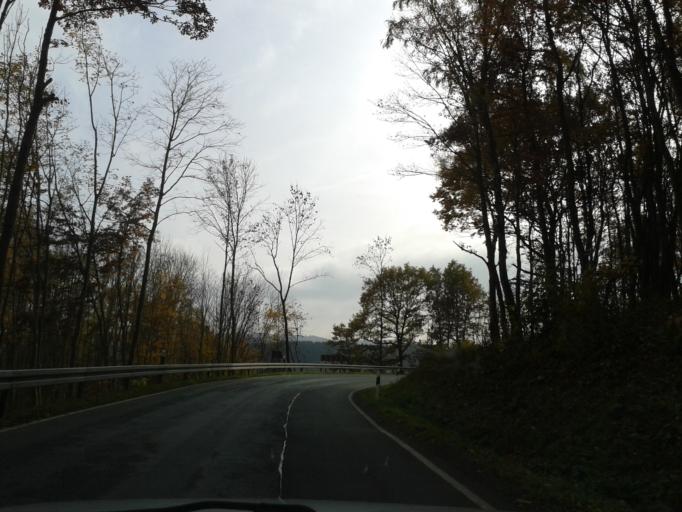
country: DE
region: North Rhine-Westphalia
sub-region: Regierungsbezirk Arnsberg
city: Bad Laasphe
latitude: 50.8631
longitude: 8.3747
